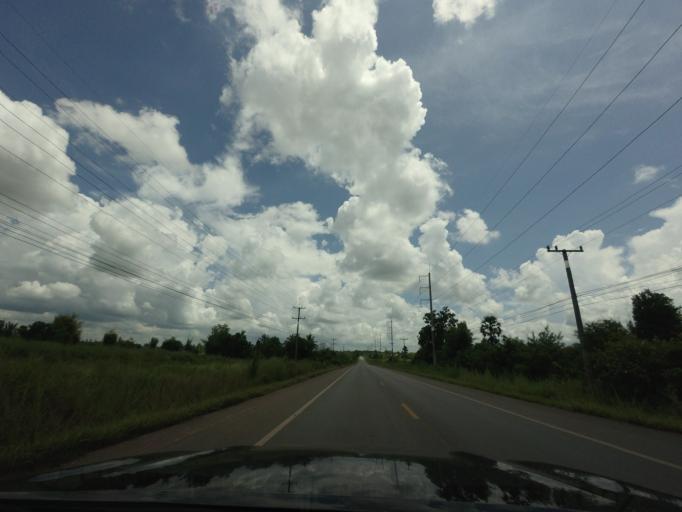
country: TH
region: Nong Khai
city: Sa Khrai
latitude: 17.5542
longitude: 102.7081
